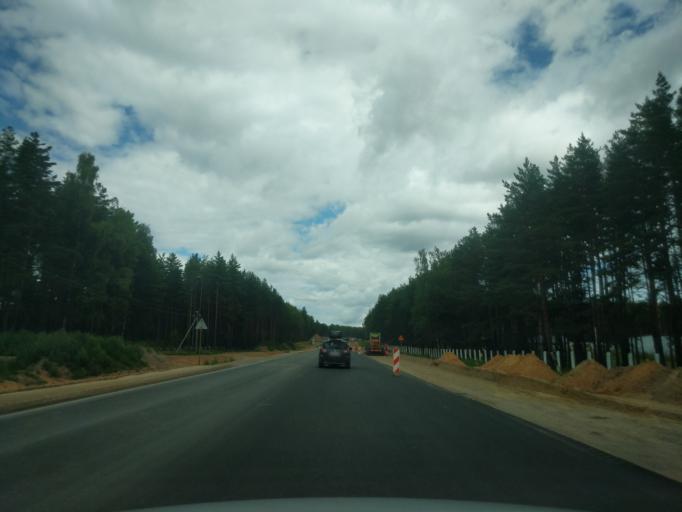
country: RU
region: Jaroslavl
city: Levashevo
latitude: 57.6786
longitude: 40.5925
